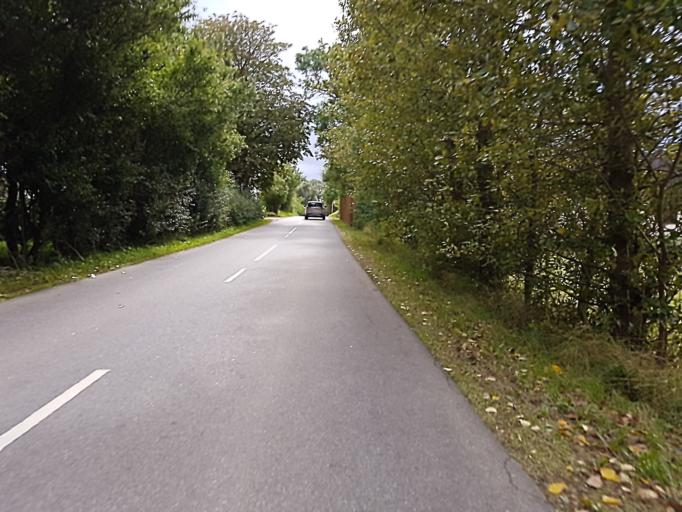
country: DK
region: Zealand
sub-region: Roskilde Kommune
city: Gundsomagle
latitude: 55.7249
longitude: 12.1388
